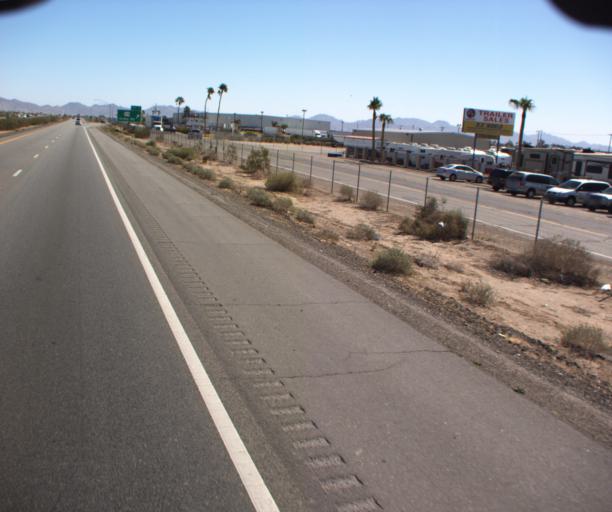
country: US
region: Arizona
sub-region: Yuma County
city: Yuma
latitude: 32.6764
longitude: -114.5303
